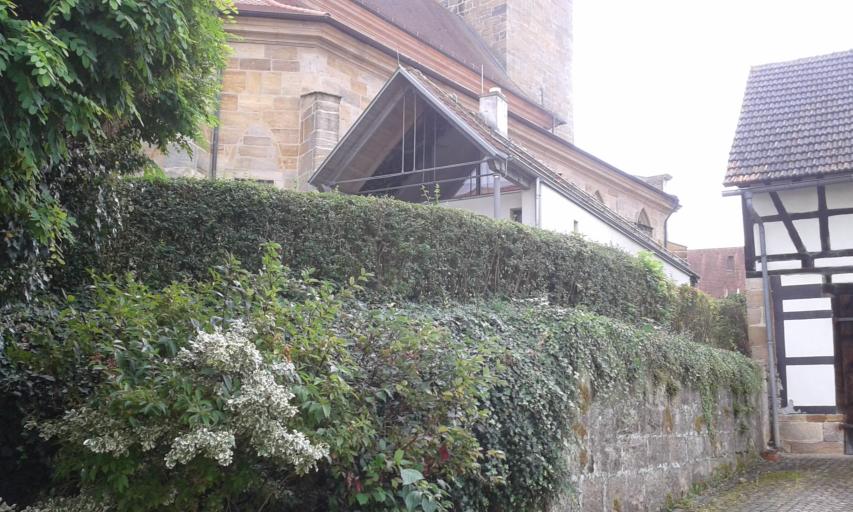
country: DE
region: Bavaria
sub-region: Regierungsbezirk Unterfranken
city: Rentweinsdorf
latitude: 50.0952
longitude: 10.7943
